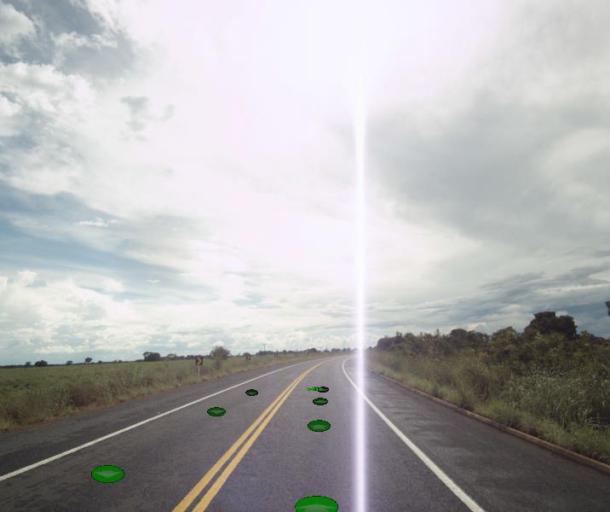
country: BR
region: Goias
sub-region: Sao Miguel Do Araguaia
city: Sao Miguel do Araguaia
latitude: -13.2849
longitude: -50.4894
